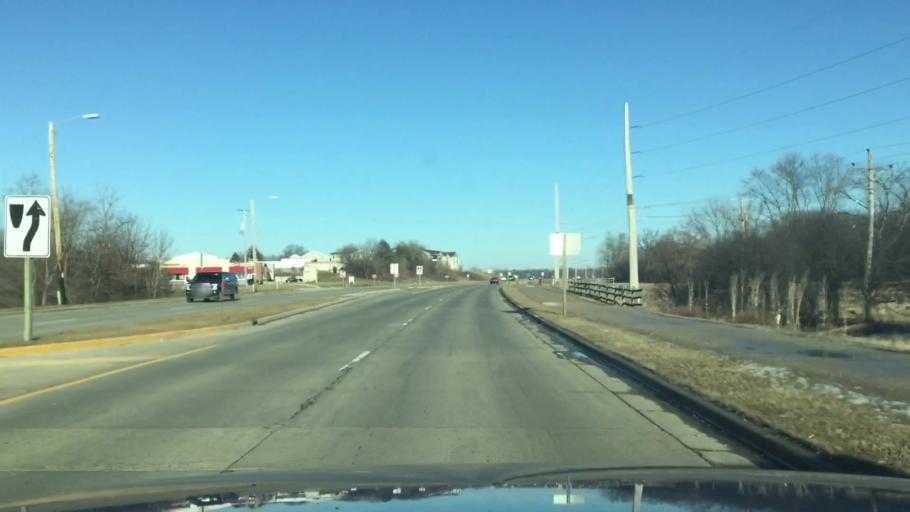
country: US
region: Wisconsin
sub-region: Racine County
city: Burlington
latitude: 42.6961
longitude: -88.2612
